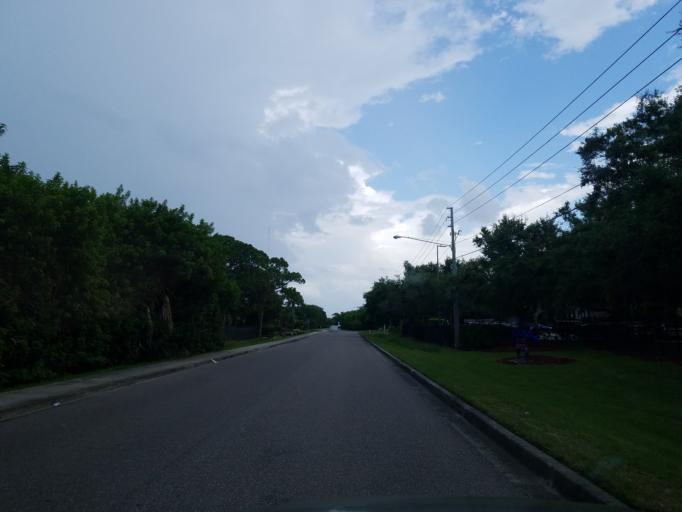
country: US
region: Florida
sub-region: Pinellas County
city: Gandy
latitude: 27.8738
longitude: -82.6357
